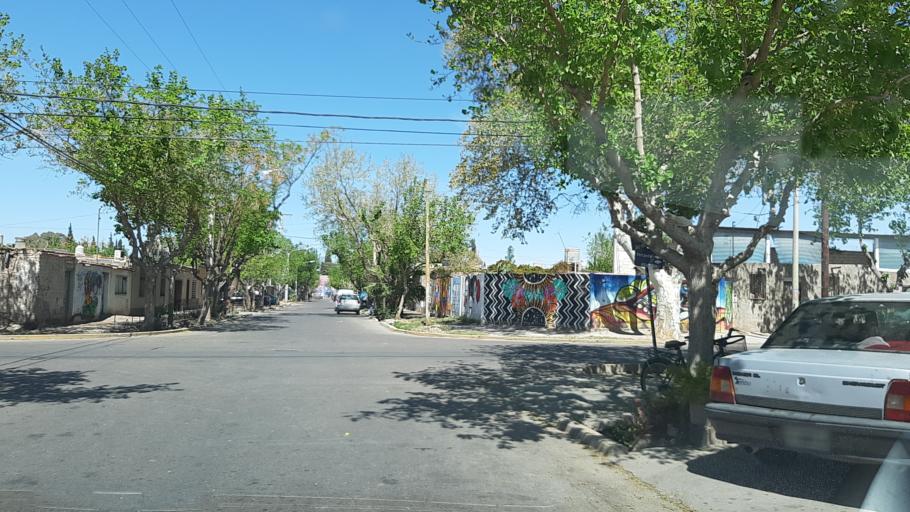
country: AR
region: San Juan
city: San Juan
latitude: -31.5238
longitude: -68.5407
